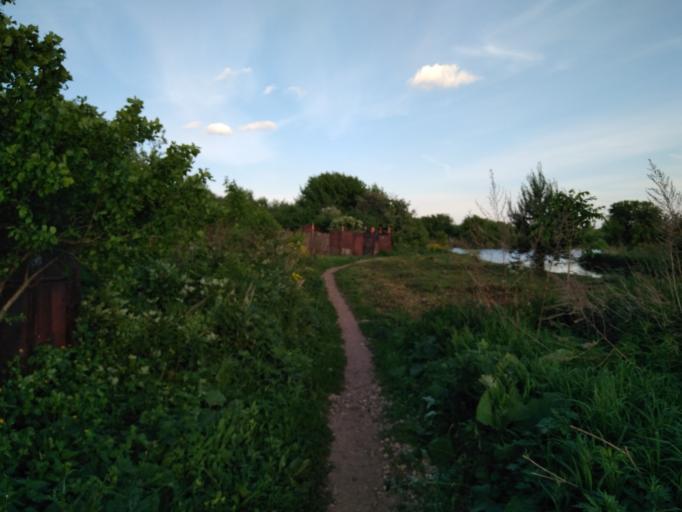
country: RU
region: Moskovskaya
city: Zhukovskiy
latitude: 55.5831
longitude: 38.0992
